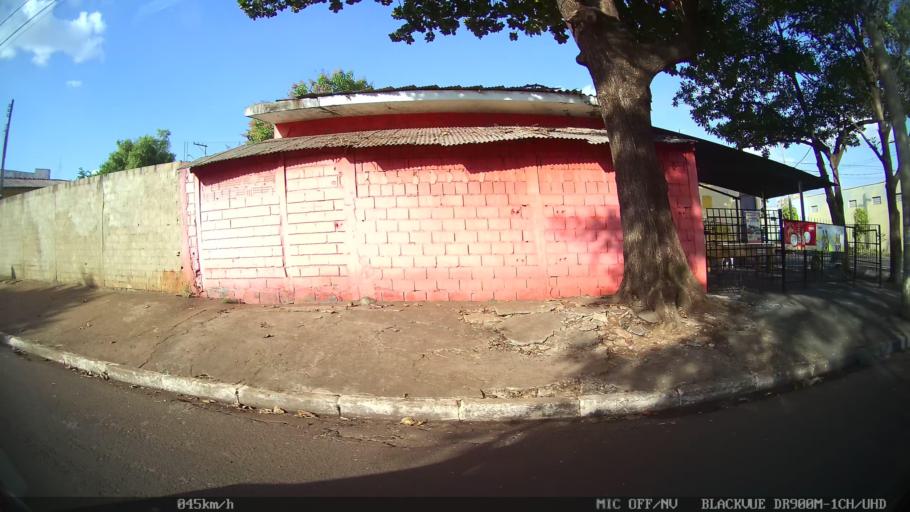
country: BR
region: Sao Paulo
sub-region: Ribeirao Preto
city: Ribeirao Preto
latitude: -21.1456
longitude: -47.7993
